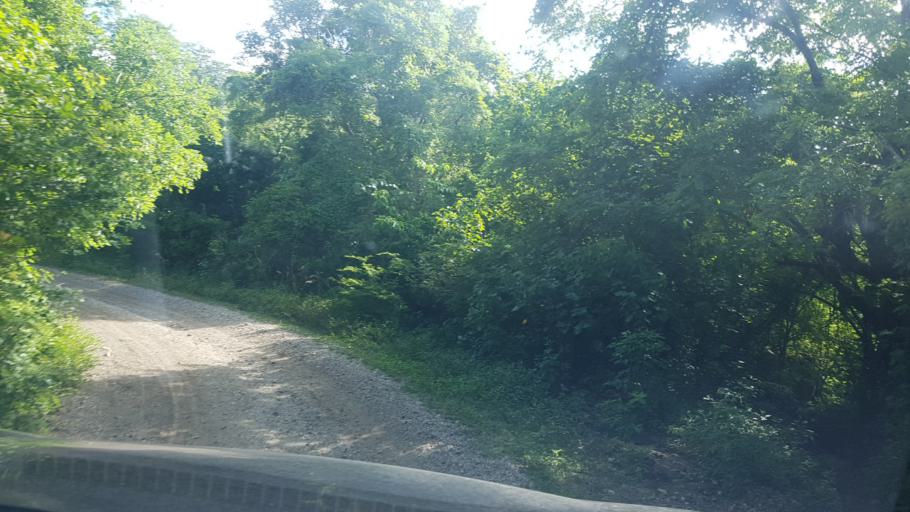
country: NI
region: Nueva Segovia
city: Ocotal
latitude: 13.6105
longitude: -86.4516
